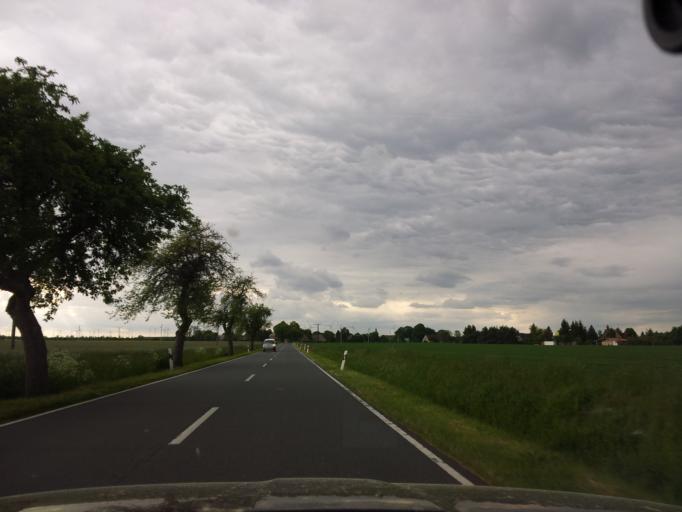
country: DE
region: Brandenburg
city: Niedergorsdorf
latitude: 51.9803
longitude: 12.9545
